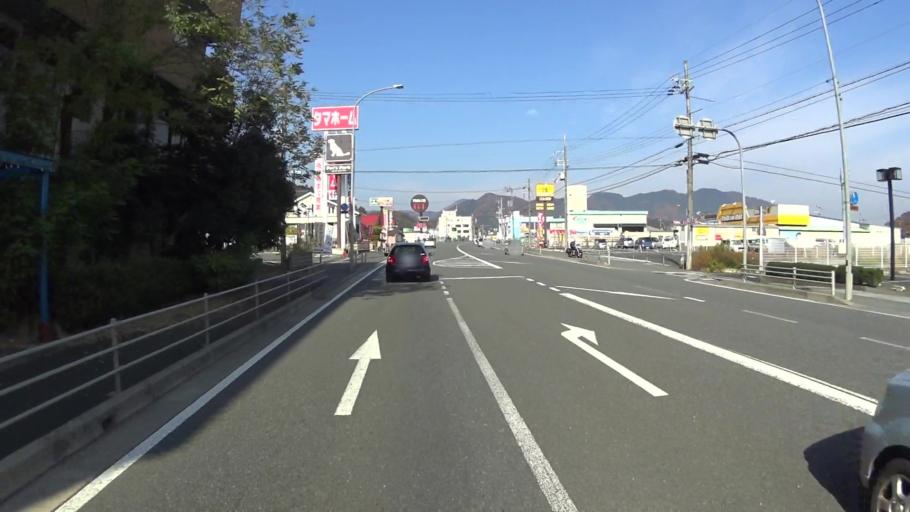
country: JP
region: Kyoto
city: Fukuchiyama
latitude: 35.3188
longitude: 135.0990
